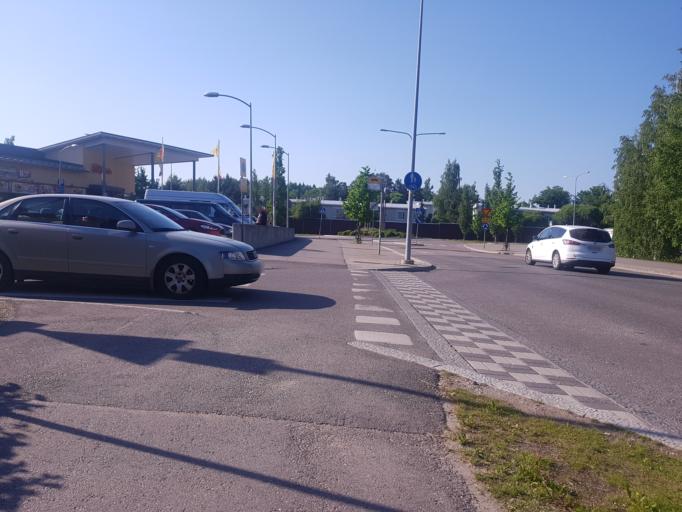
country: FI
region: Uusimaa
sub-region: Helsinki
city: Vantaa
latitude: 60.2671
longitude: 25.0149
